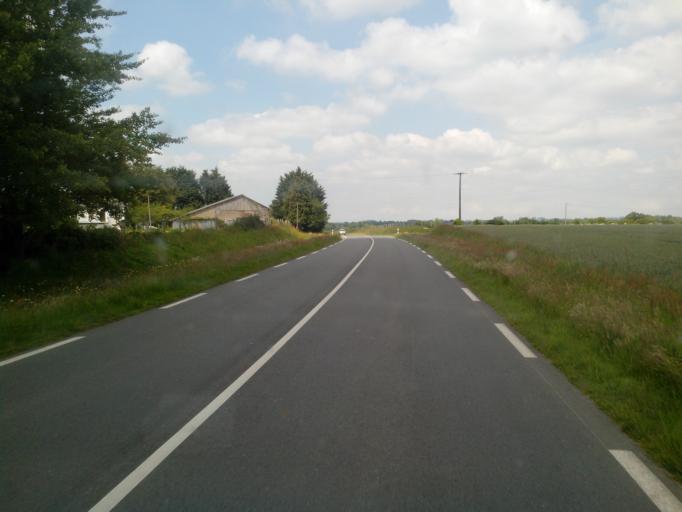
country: FR
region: Brittany
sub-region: Departement d'Ille-et-Vilaine
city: Saint-Germain-en-Cogles
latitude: 48.3754
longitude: -1.2490
